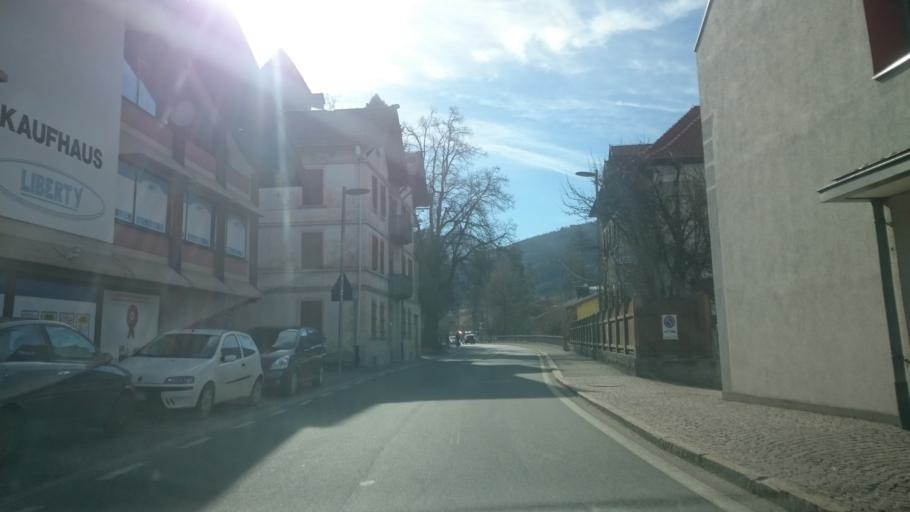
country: IT
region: Trentino-Alto Adige
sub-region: Bolzano
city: Monguelfo
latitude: 46.7559
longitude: 12.1058
